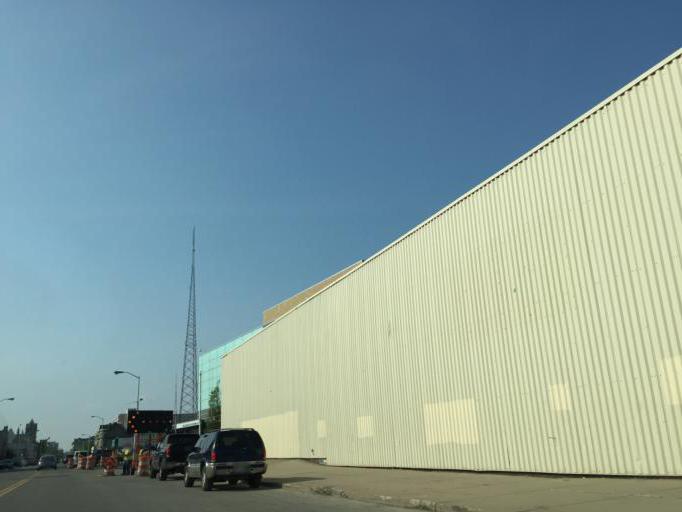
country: US
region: Michigan
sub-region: Wayne County
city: Detroit
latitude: 42.3475
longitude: -83.0618
